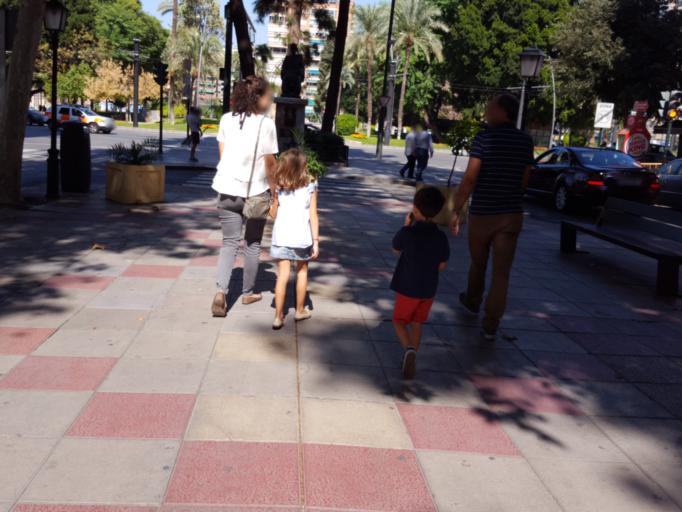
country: ES
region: Murcia
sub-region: Murcia
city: Murcia
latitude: 37.9912
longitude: -1.1304
